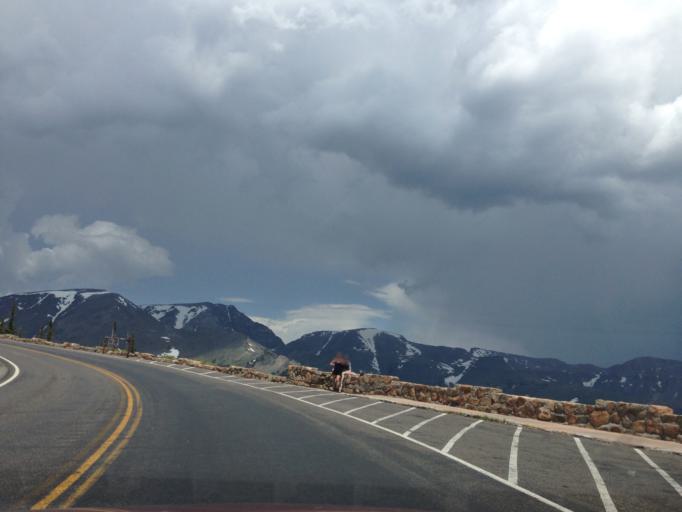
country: US
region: Colorado
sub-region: Larimer County
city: Estes Park
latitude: 40.4010
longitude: -105.6639
